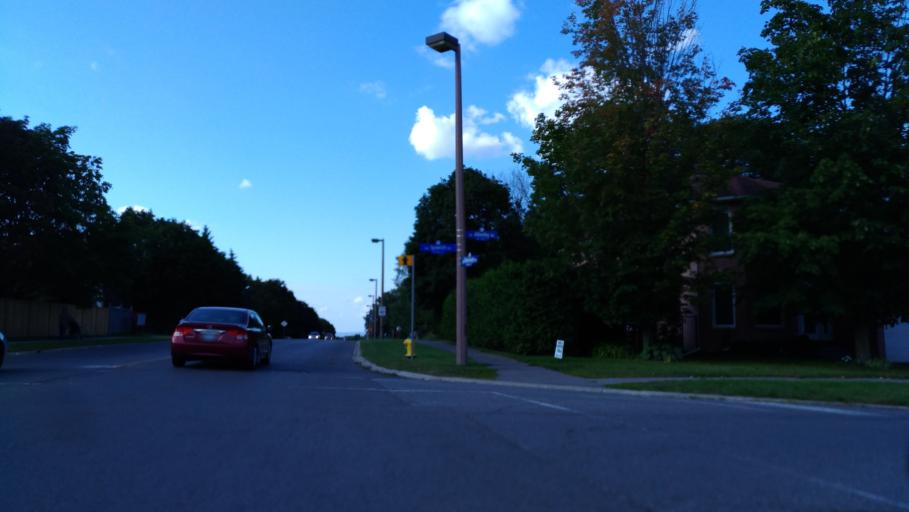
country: CA
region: Ontario
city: Bells Corners
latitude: 45.3461
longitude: -75.9318
